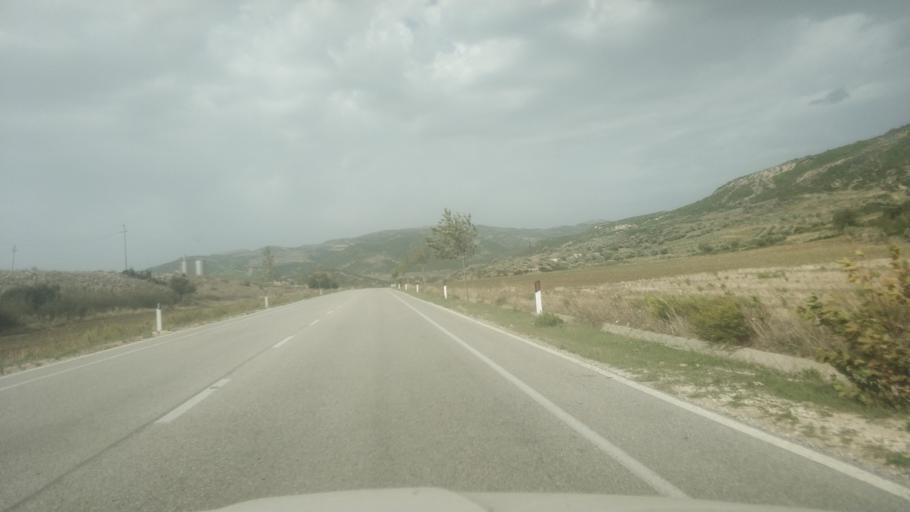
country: AL
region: Gjirokaster
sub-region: Rrethi i Tepelenes
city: Memaliaj
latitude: 40.3684
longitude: 19.9083
